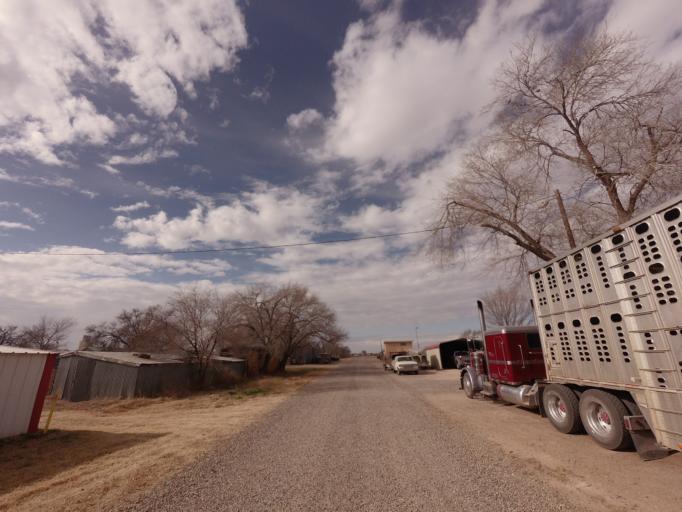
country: US
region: New Mexico
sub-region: Curry County
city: Clovis
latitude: 34.3939
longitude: -103.2161
